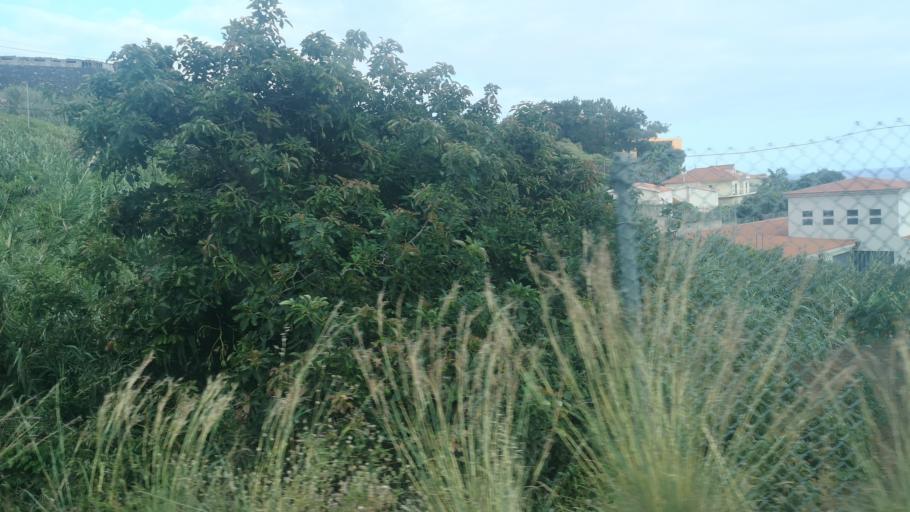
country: PT
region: Madeira
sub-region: Santa Cruz
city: Camacha
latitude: 32.6532
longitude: -16.8210
